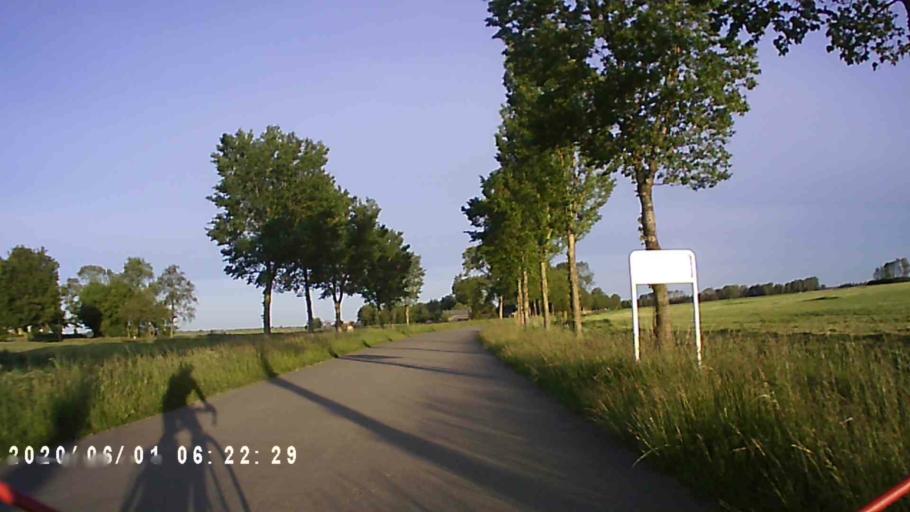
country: NL
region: Friesland
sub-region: Gemeente Kollumerland en Nieuwkruisland
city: Kollum
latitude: 53.2651
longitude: 6.2227
